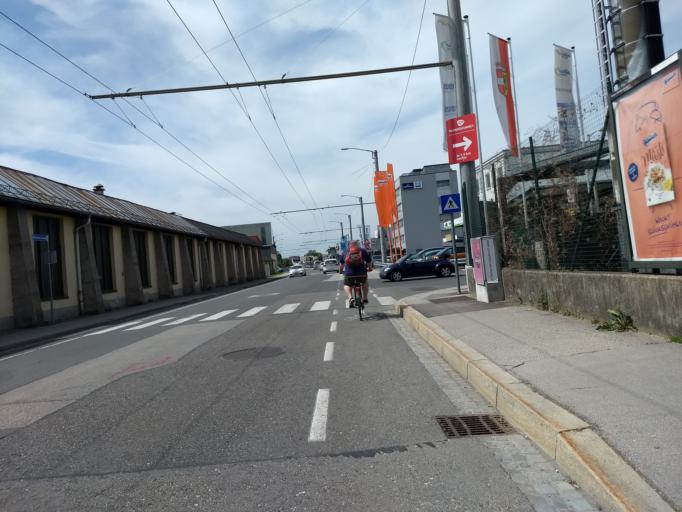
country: AT
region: Salzburg
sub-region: Salzburg Stadt
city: Salzburg
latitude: 47.8048
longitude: 13.0125
